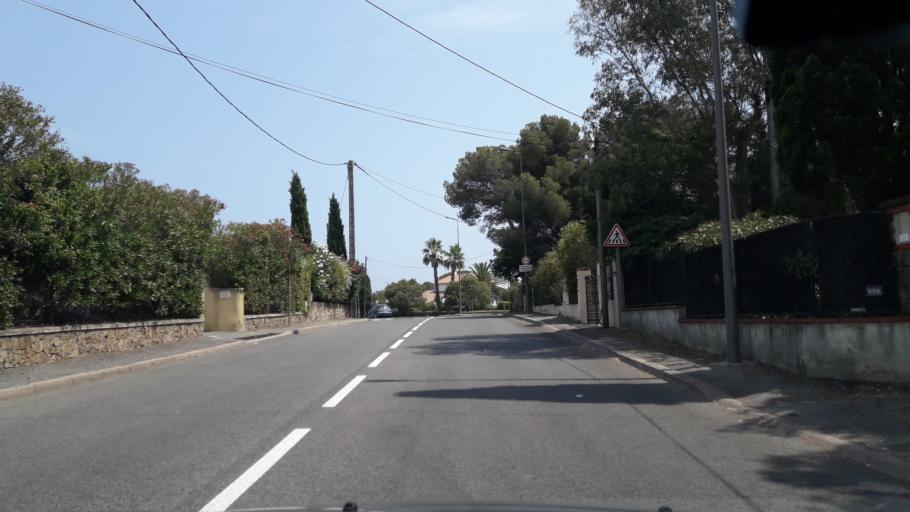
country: FR
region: Provence-Alpes-Cote d'Azur
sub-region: Departement du Var
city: Saint-Raphael
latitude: 43.4201
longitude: 6.7879
